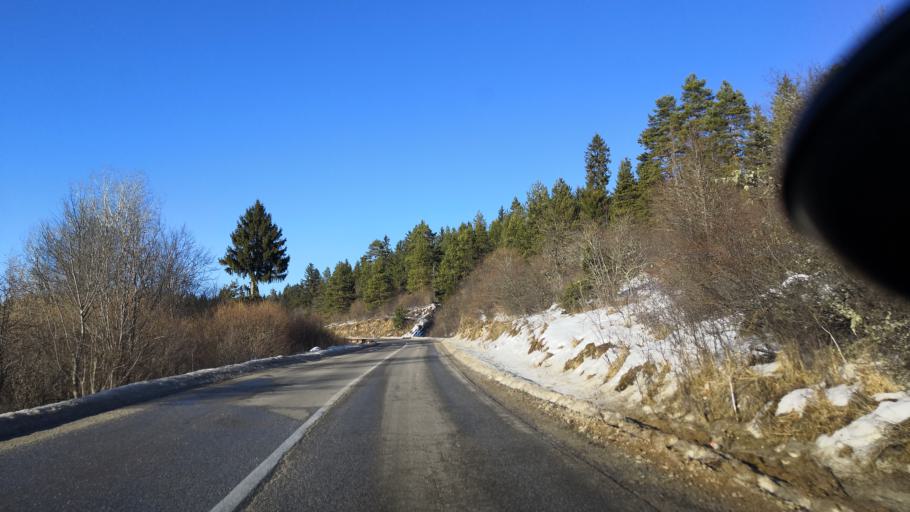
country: BA
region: Republika Srpska
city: Han Pijesak
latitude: 44.0189
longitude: 18.8834
